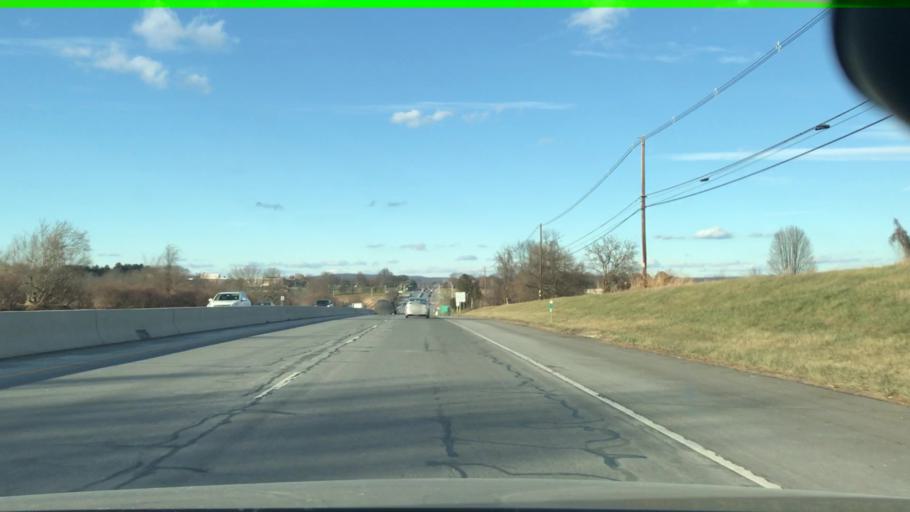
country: US
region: New Jersey
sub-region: Hunterdon County
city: Annandale
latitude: 40.6190
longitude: -74.8797
